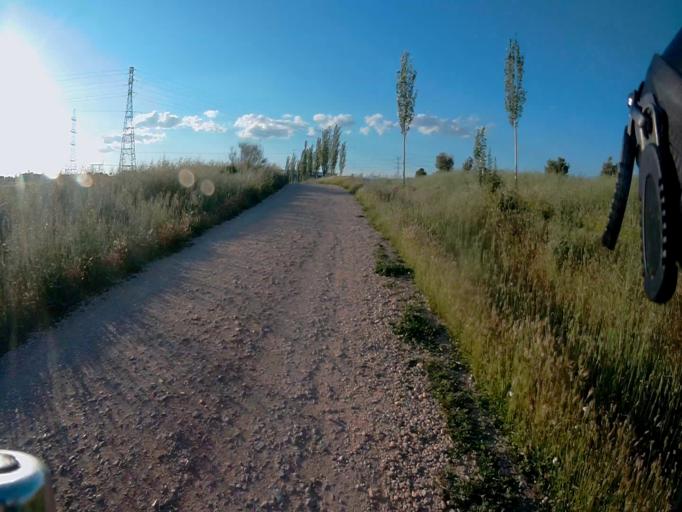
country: ES
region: Madrid
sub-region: Provincia de Madrid
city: Fuenlabrada
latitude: 40.3001
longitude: -3.7976
